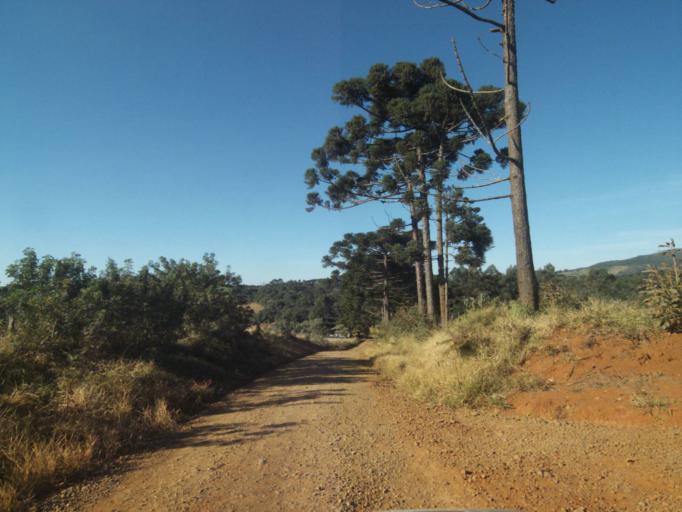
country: BR
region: Parana
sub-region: Tibagi
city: Tibagi
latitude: -24.5422
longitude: -50.5062
